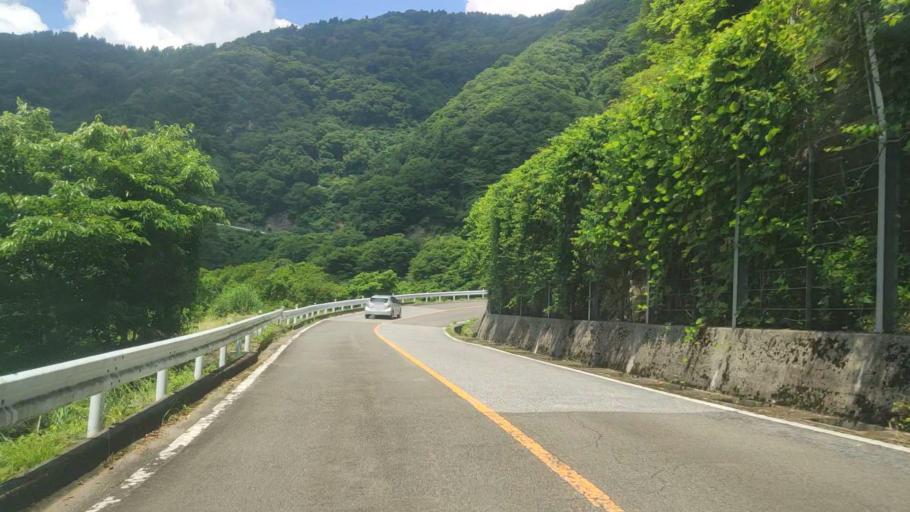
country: JP
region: Gifu
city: Tarui
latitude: 35.3898
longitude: 136.4390
